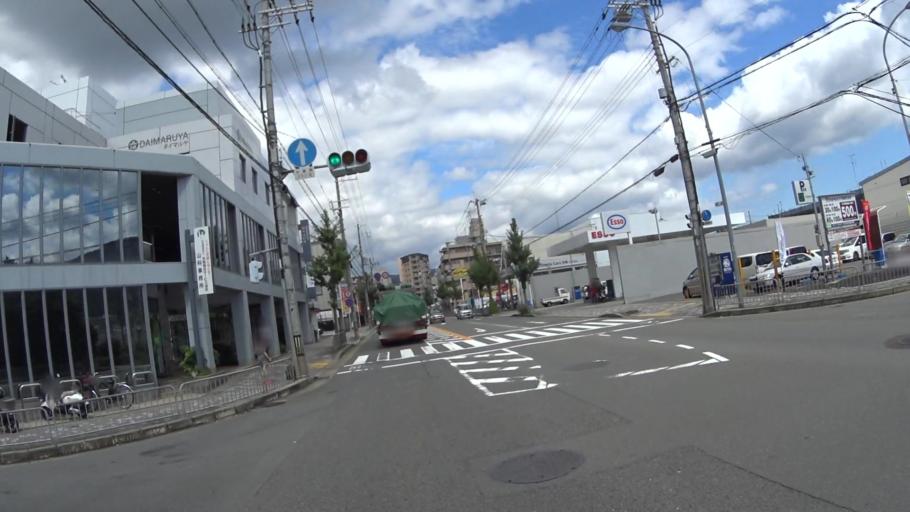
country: JP
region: Shiga Prefecture
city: Otsu-shi
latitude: 34.9680
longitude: 135.8135
